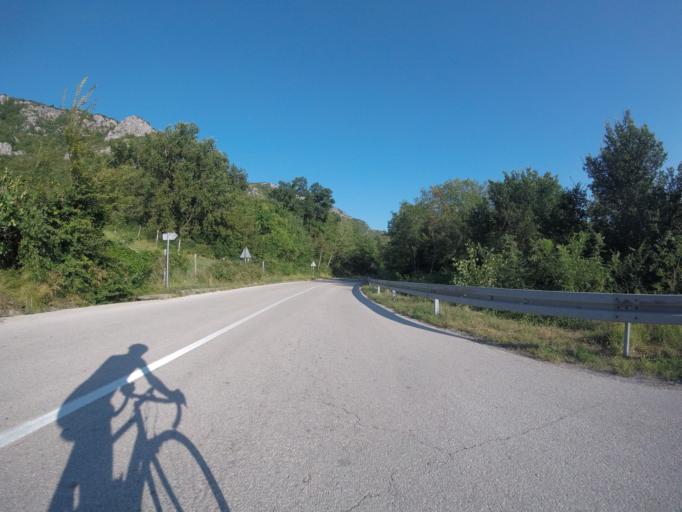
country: HR
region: Primorsko-Goranska
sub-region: Grad Crikvenica
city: Crikvenica
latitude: 45.2055
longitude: 14.7146
